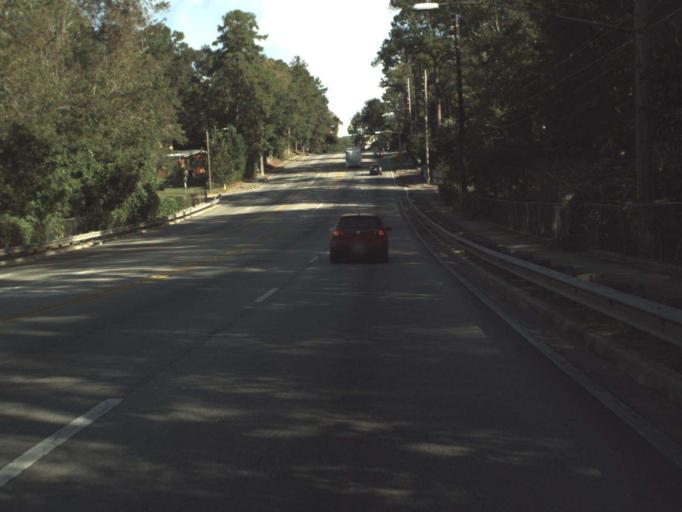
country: US
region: Florida
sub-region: Leon County
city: Tallahassee
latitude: 30.4507
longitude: -84.2627
